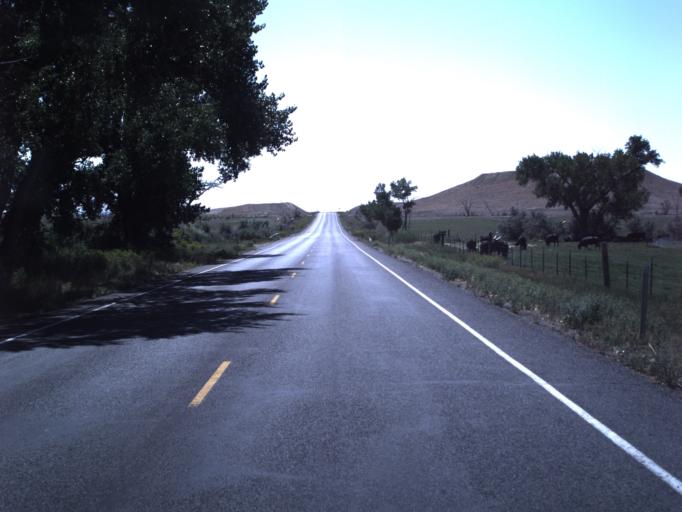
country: US
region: Utah
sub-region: Emery County
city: Castle Dale
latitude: 39.1886
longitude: -111.0477
